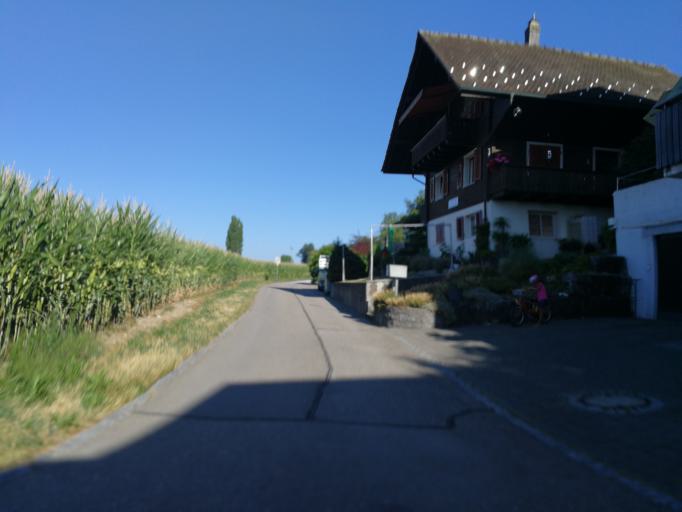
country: CH
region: Zurich
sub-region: Bezirk Hinwil
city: Wolfhausen
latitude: 47.2550
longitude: 8.7905
